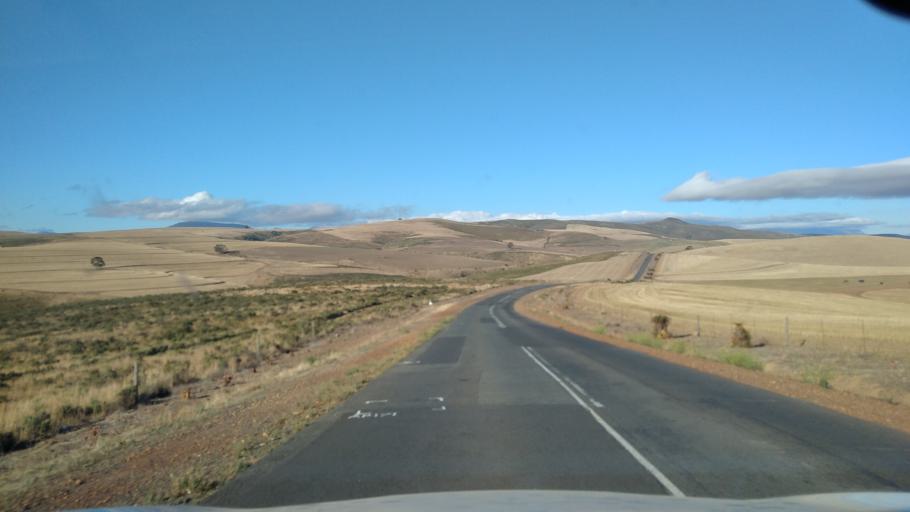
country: ZA
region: Western Cape
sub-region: Overberg District Municipality
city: Caledon
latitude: -34.1751
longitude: 19.2810
